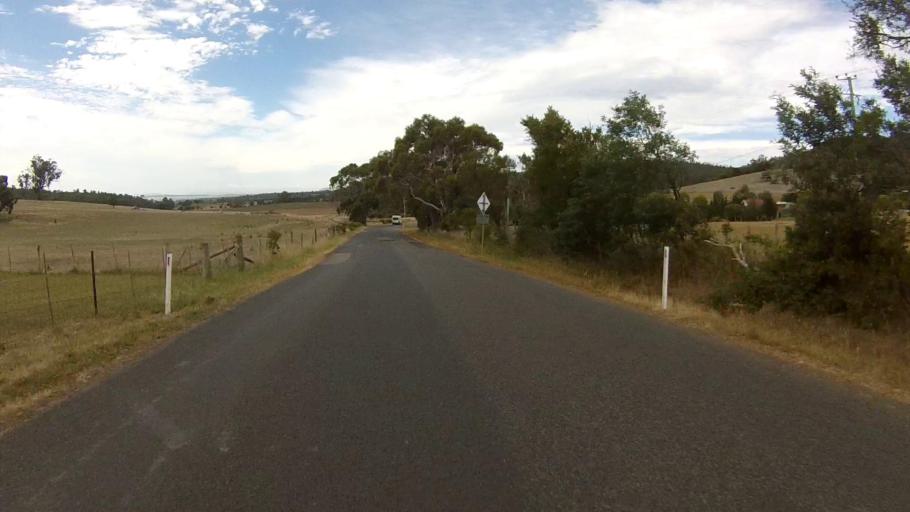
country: AU
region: Tasmania
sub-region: Clarence
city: Lindisfarne
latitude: -42.7435
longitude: 147.3683
